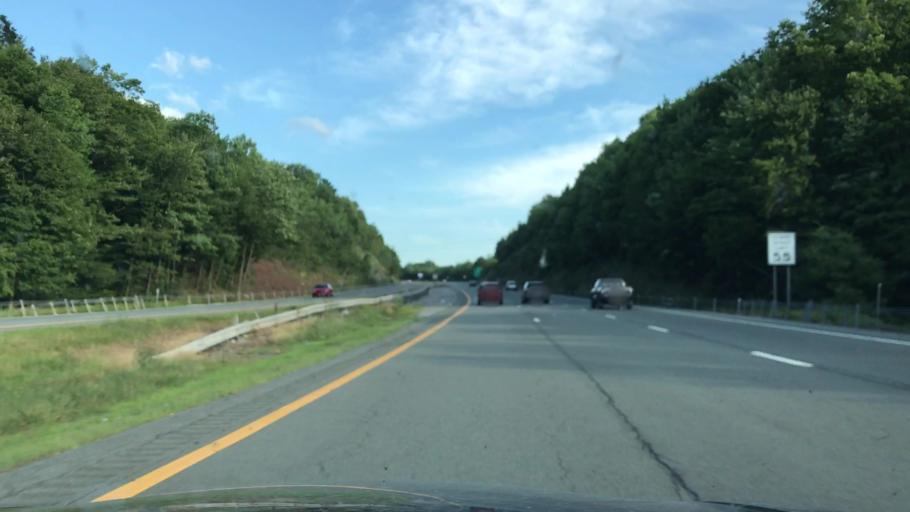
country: US
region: New York
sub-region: Sullivan County
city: Monticello
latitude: 41.6759
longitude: -74.7156
